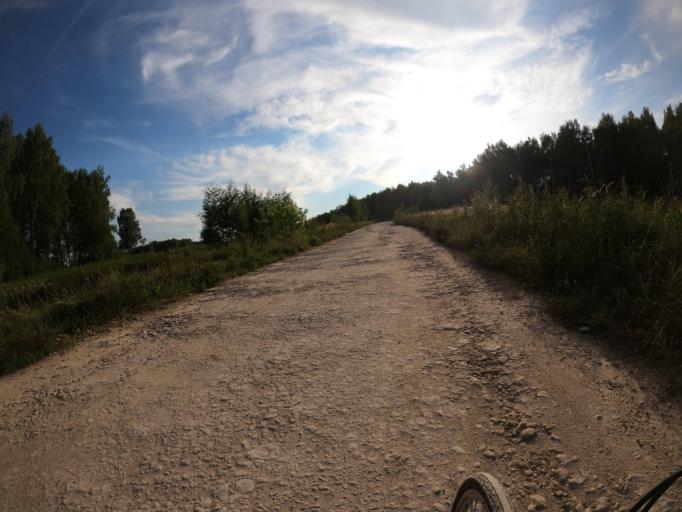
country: RU
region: Moskovskaya
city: Meshcherino
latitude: 55.1352
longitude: 38.3928
